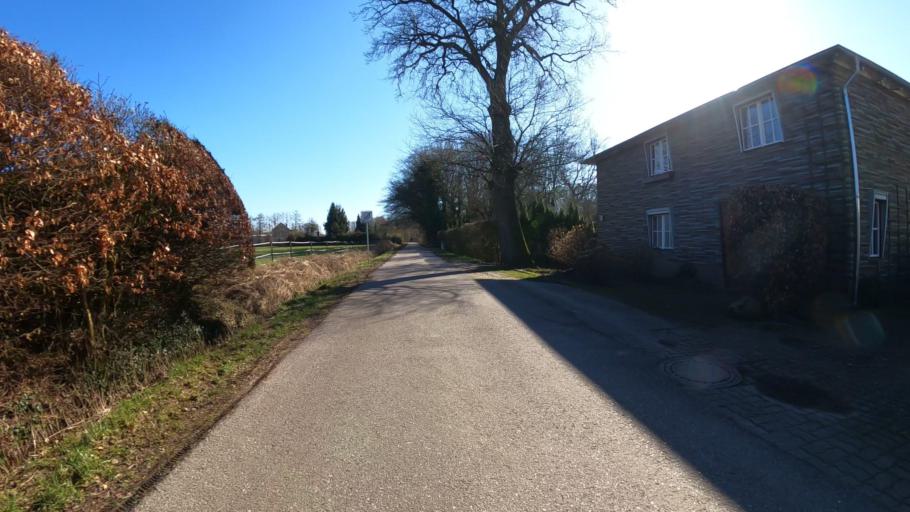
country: DE
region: Schleswig-Holstein
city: Kummerfeld
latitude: 53.6850
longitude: 9.7762
